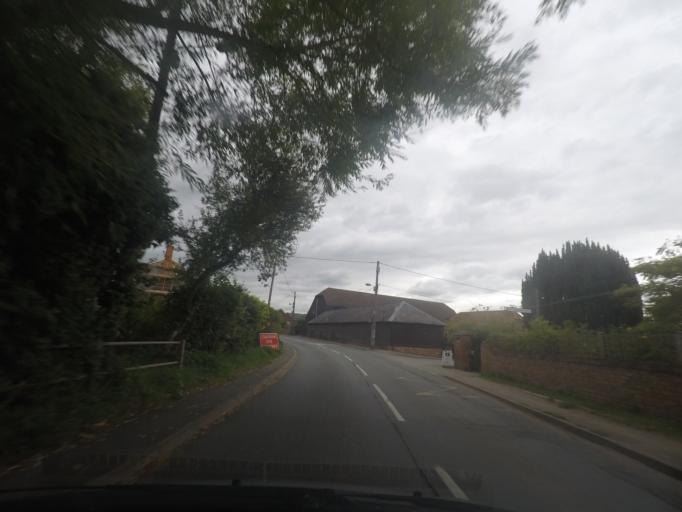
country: GB
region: England
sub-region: Oxfordshire
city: Harwell
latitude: 51.6253
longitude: -1.3014
